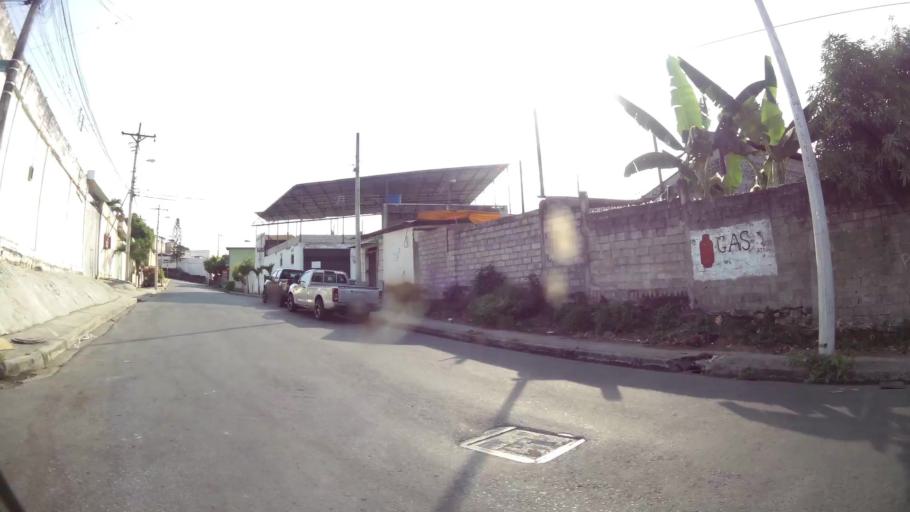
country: EC
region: Guayas
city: Guayaquil
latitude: -2.1422
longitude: -79.9292
